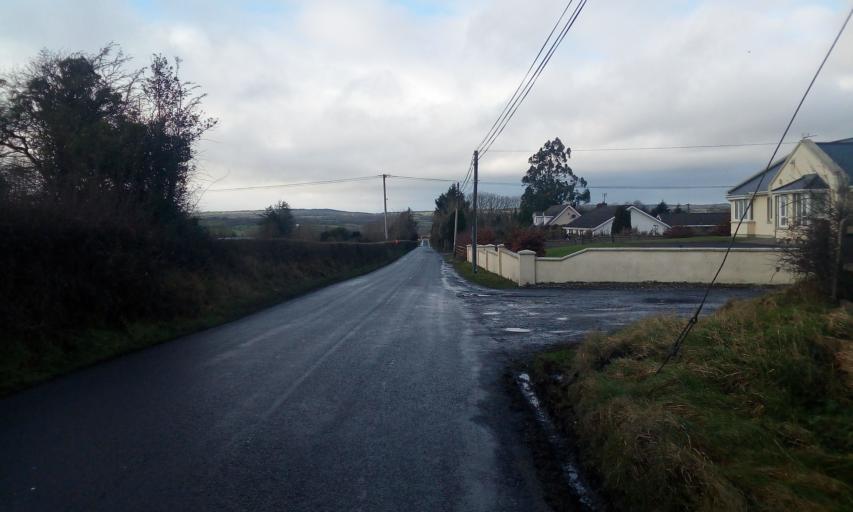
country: IE
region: Leinster
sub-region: Kilkenny
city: Castlecomer
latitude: 52.7999
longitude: -7.1896
